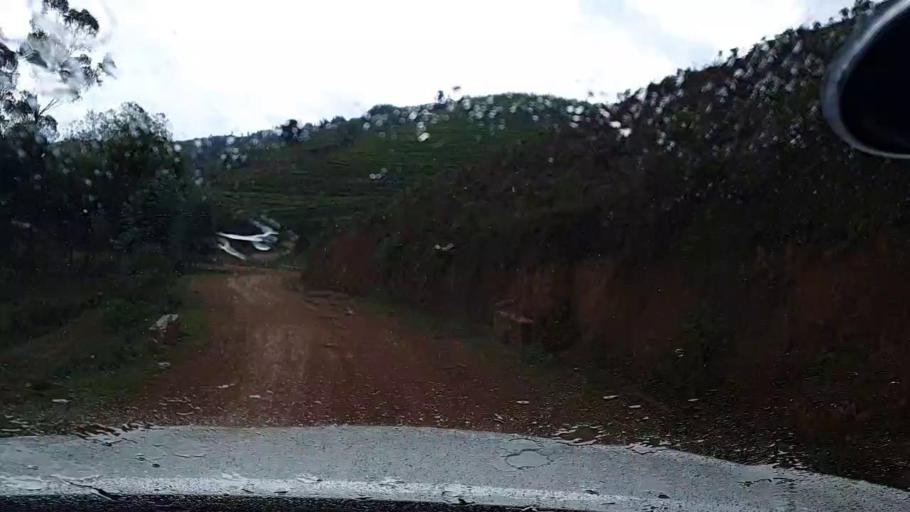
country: RW
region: Western Province
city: Kibuye
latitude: -2.1609
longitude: 29.4354
